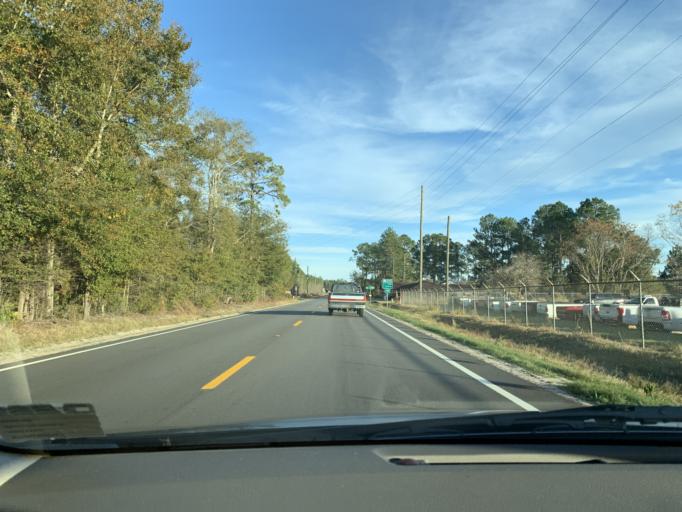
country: US
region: Georgia
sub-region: Irwin County
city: Ocilla
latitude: 31.5910
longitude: -83.0967
